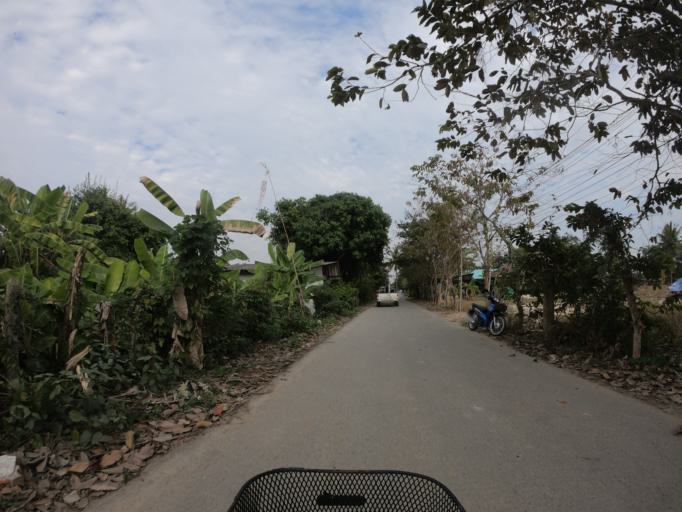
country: TH
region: Chiang Mai
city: San Sai
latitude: 18.7992
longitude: 99.0513
